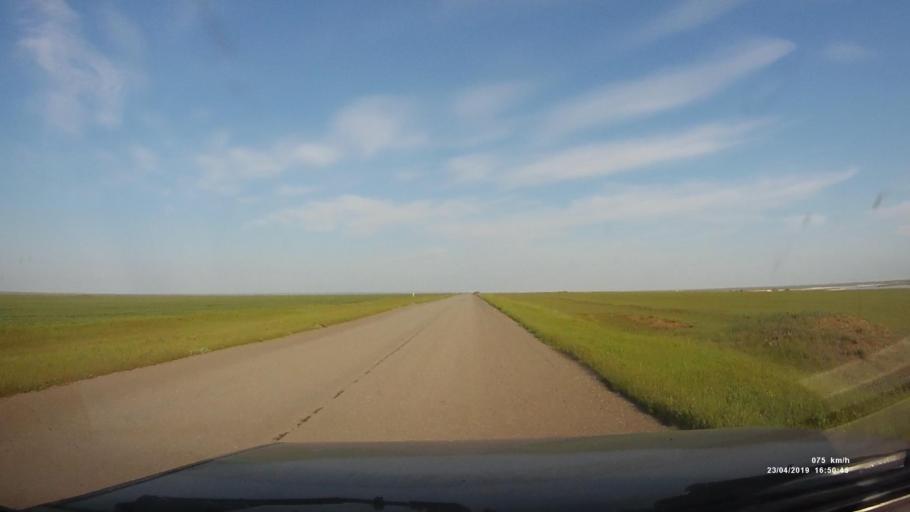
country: RU
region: Kalmykiya
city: Priyutnoye
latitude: 46.3258
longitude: 43.2961
